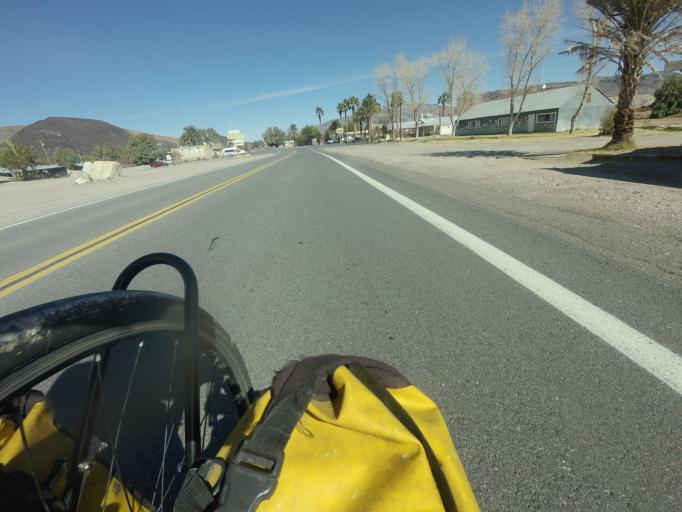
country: US
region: Nevada
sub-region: Nye County
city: Pahrump
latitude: 35.9738
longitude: -116.2703
